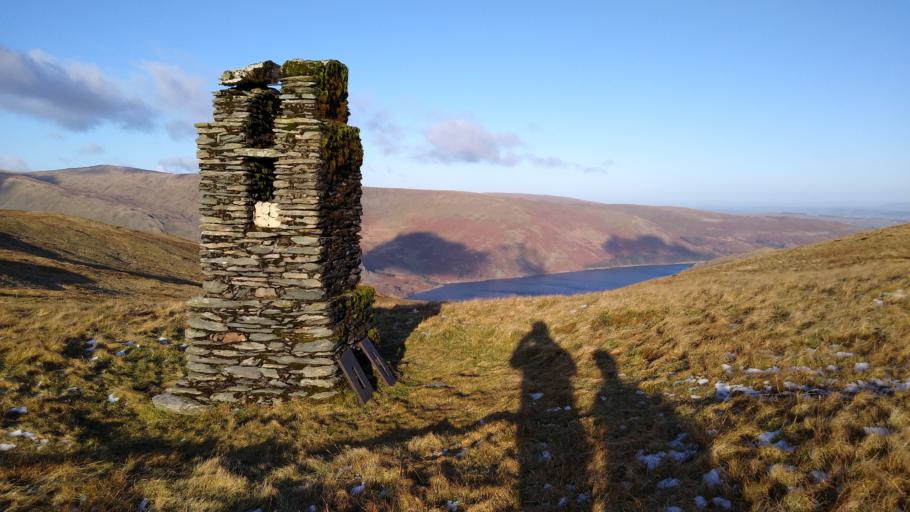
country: GB
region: England
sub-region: Cumbria
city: Windermere
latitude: 54.4850
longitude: -2.7981
